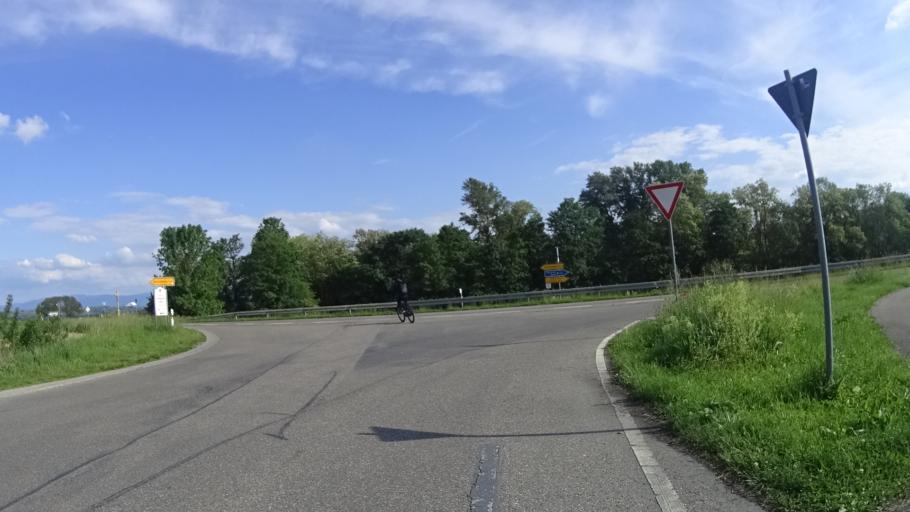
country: DE
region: Baden-Wuerttemberg
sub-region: Freiburg Region
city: Breisach am Rhein
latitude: 48.0160
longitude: 7.6139
